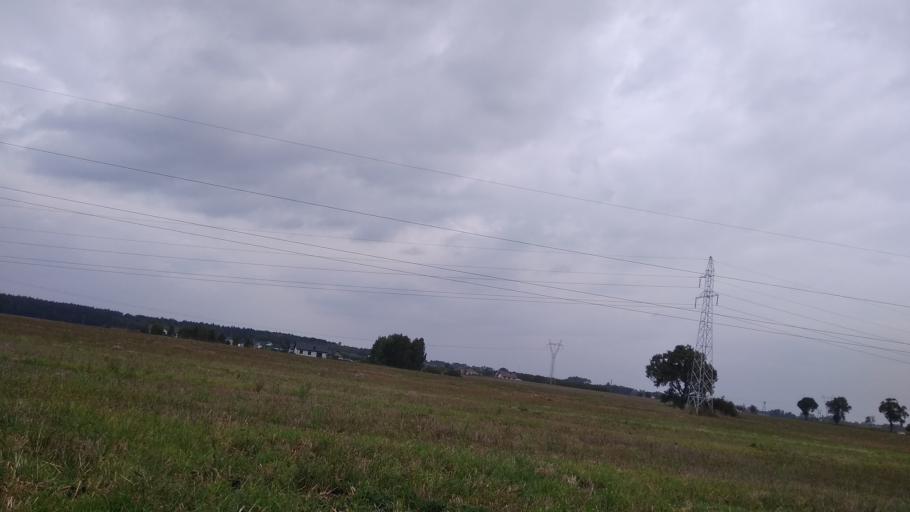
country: PL
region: Kujawsko-Pomorskie
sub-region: Powiat bydgoski
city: Osielsko
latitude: 53.2117
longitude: 18.1446
